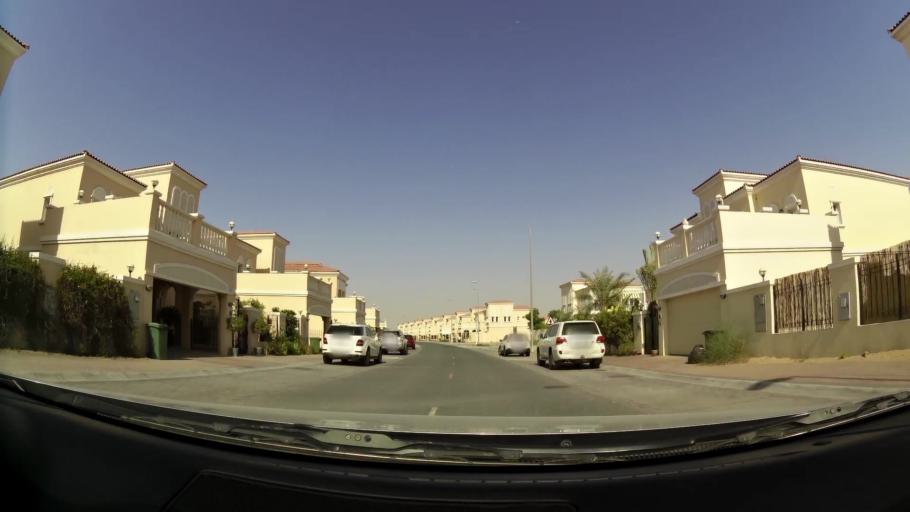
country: AE
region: Dubai
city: Dubai
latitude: 25.0718
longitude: 55.2117
